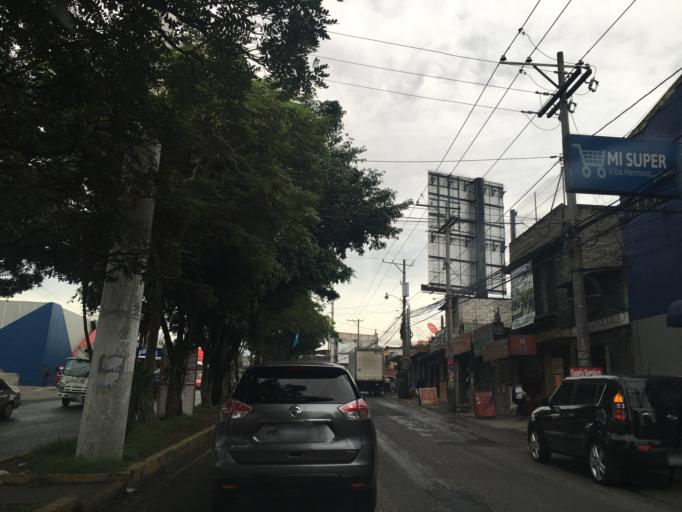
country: GT
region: Guatemala
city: Petapa
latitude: 14.5254
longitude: -90.5520
